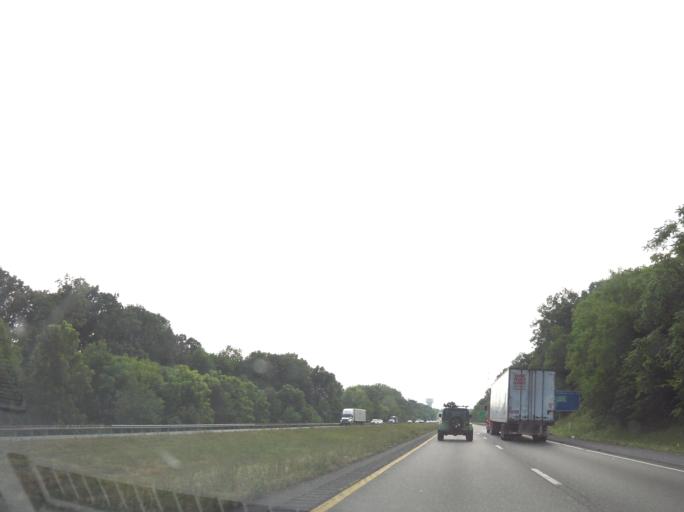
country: US
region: Maryland
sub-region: Washington County
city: Williamsport
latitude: 39.5836
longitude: -77.8564
